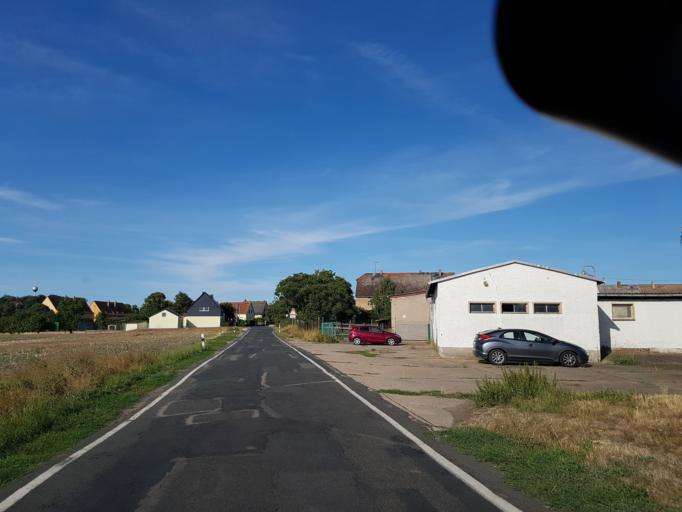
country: DE
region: Saxony
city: Naundorf
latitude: 51.2354
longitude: 13.1323
